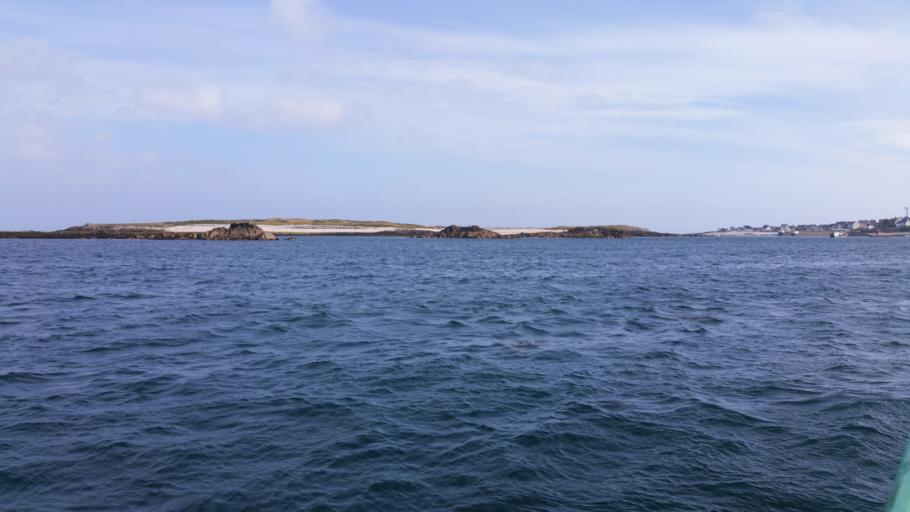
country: FR
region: Brittany
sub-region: Departement du Finistere
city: Le Conquet
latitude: 48.4069
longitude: -4.9527
